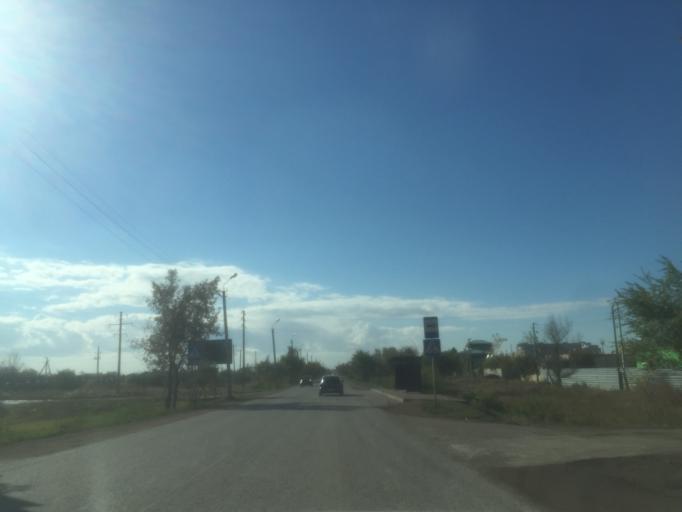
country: KZ
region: Astana Qalasy
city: Astana
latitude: 51.1994
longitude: 71.3492
